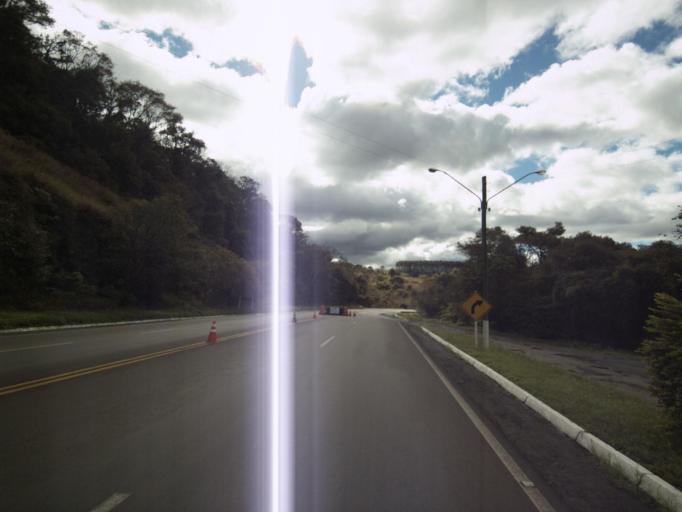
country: BR
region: Santa Catarina
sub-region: Concordia
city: Concordia
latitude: -27.3606
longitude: -51.9967
